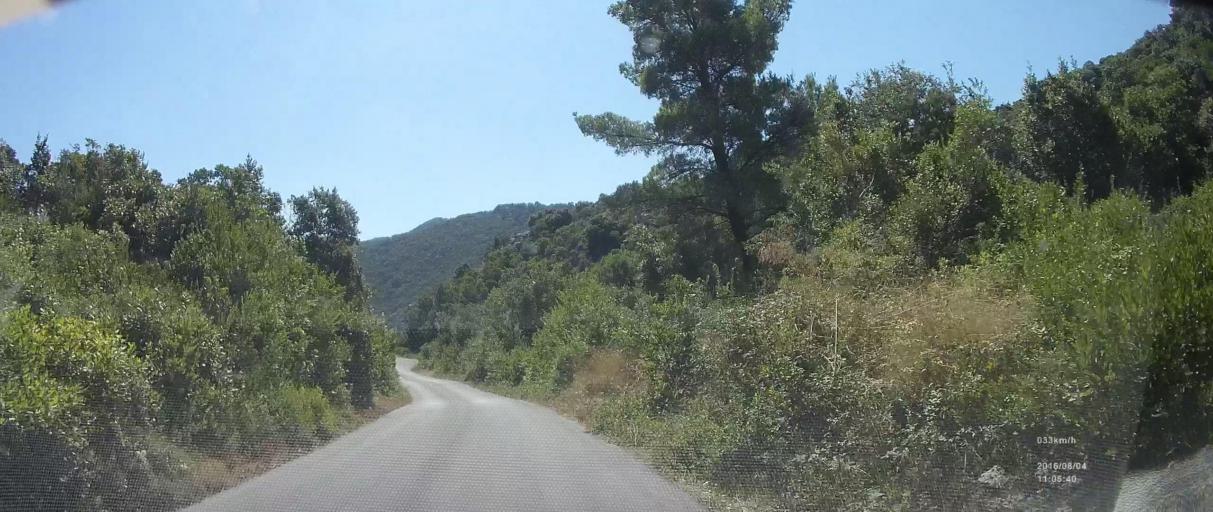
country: HR
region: Dubrovacko-Neretvanska
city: Blato
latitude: 42.7744
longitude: 17.4620
